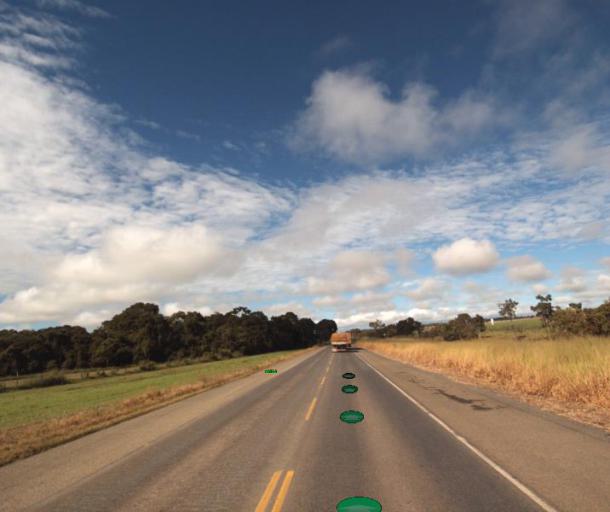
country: BR
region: Goias
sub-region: Uruacu
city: Uruacu
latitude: -14.6447
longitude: -49.1826
